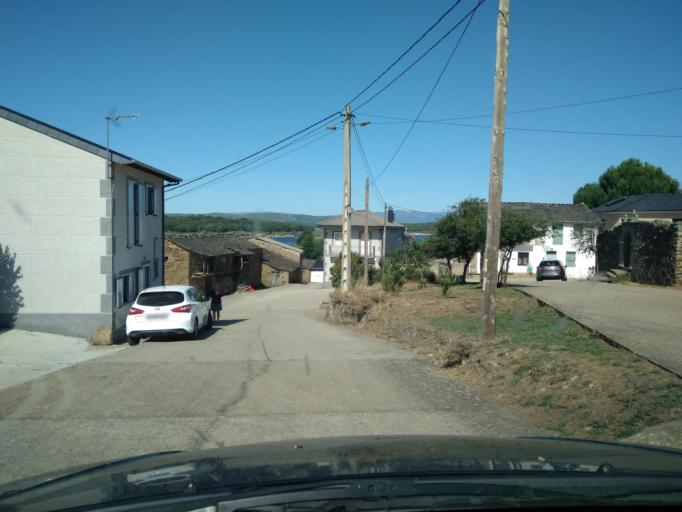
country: ES
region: Castille and Leon
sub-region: Provincia de Zamora
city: Manzanal de Arriba
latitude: 42.0075
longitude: -6.4785
